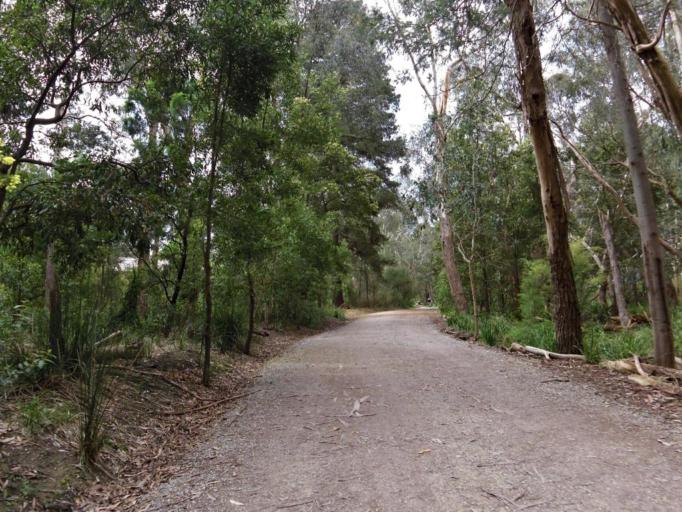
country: AU
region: Victoria
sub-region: Maroondah
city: Ringwood East
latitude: -37.7980
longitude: 145.2490
